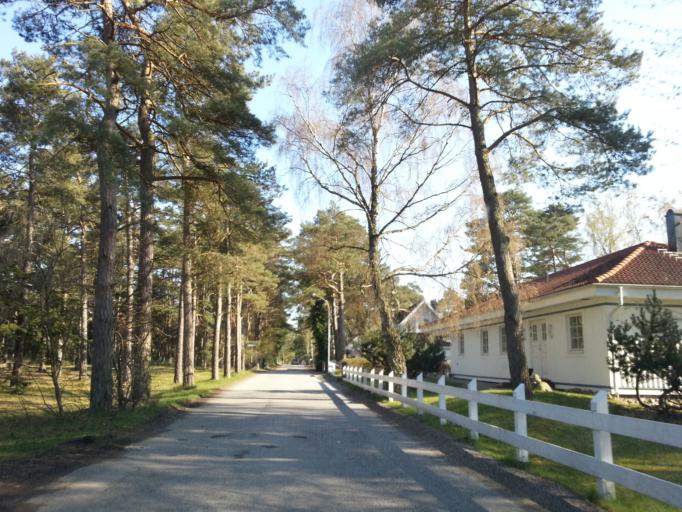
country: SE
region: Skane
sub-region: Vellinge Kommun
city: Hollviken
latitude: 55.4103
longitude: 12.9507
